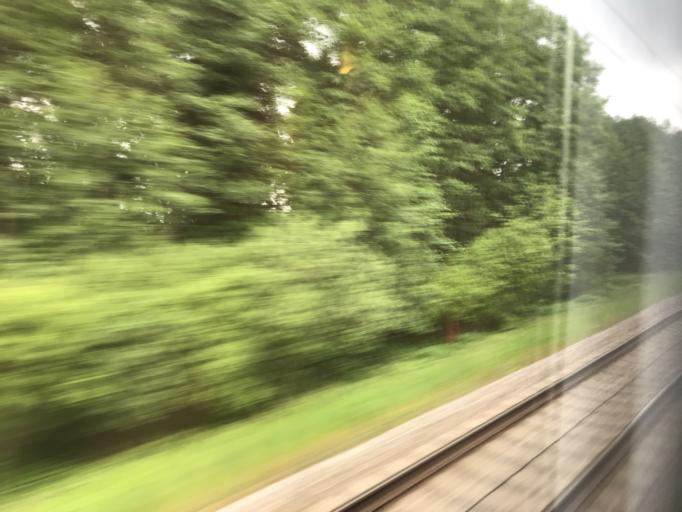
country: DE
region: Bavaria
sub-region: Swabia
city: Ustersbach
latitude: 48.3343
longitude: 10.6347
